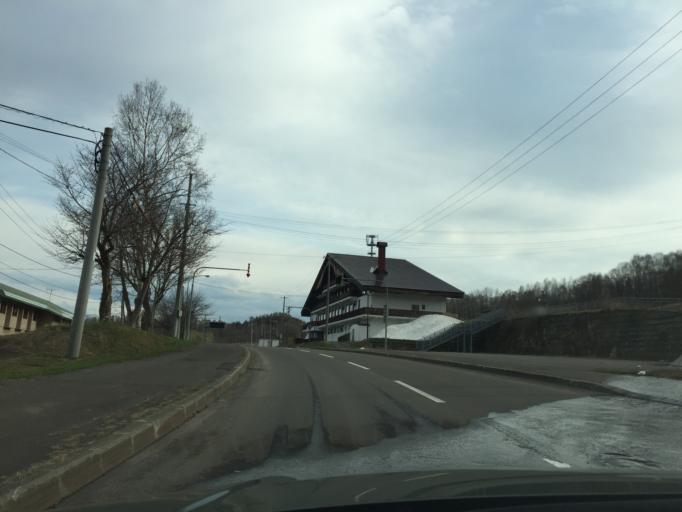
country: JP
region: Hokkaido
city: Utashinai
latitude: 43.5216
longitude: 142.0195
